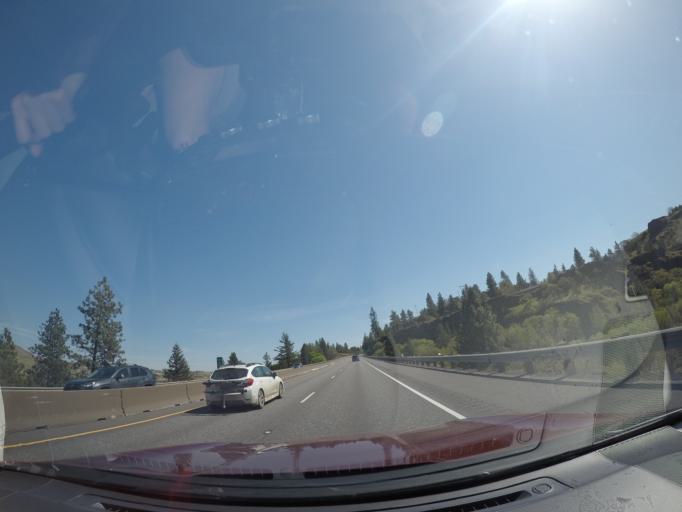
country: US
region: Oregon
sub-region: Wasco County
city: Chenoweth
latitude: 45.6596
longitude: -121.2162
